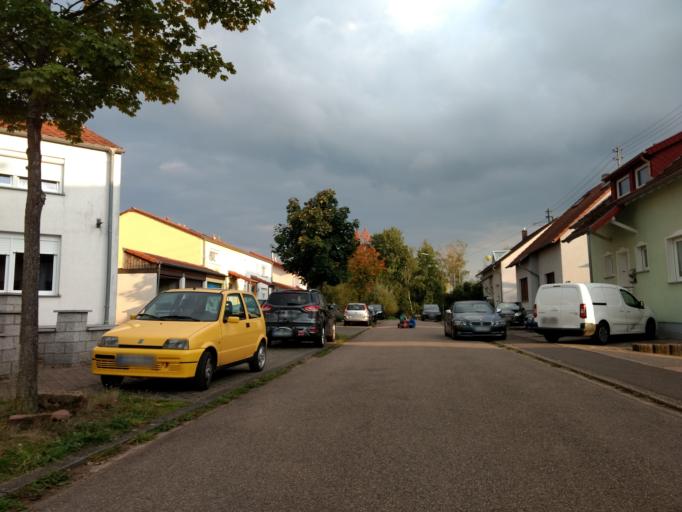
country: DE
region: Saarland
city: Rehlingen-Siersburg
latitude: 49.3742
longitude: 6.6860
